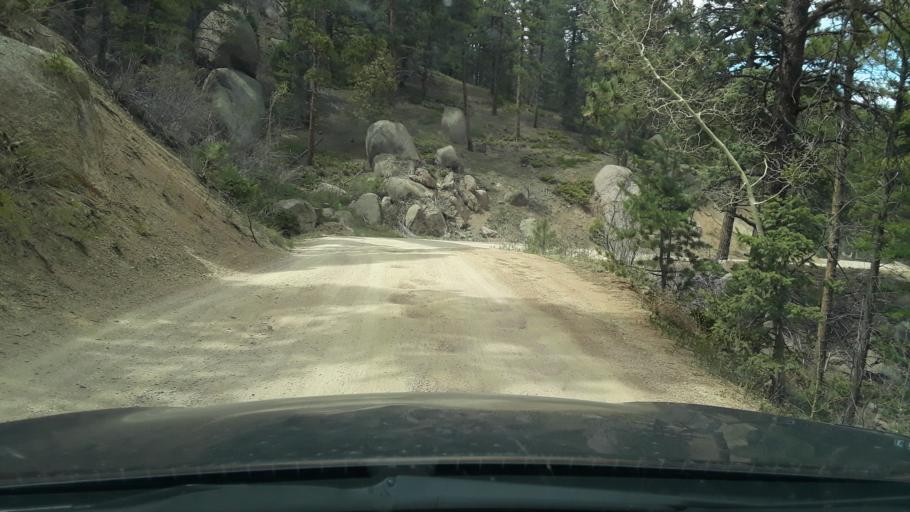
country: US
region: Colorado
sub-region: El Paso County
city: Palmer Lake
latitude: 39.0701
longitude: -104.9367
